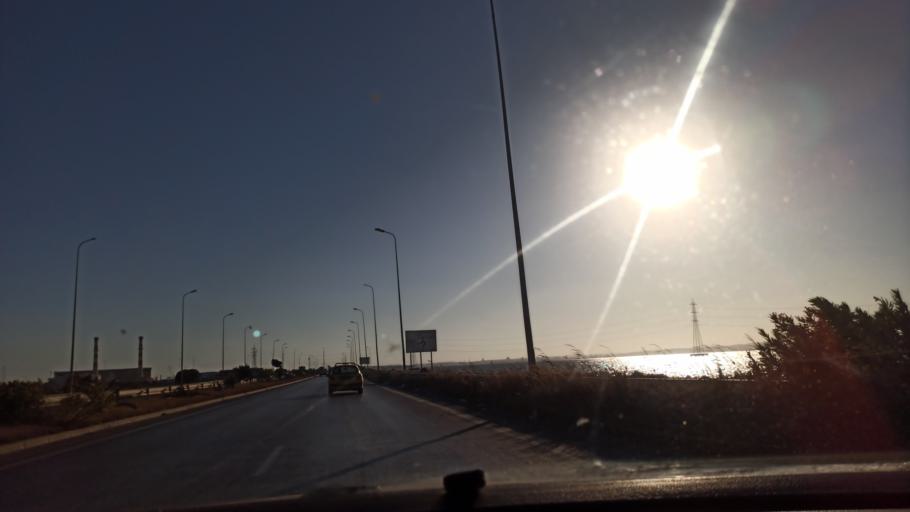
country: TN
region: Tunis
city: La Goulette
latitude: 36.8216
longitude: 10.2962
